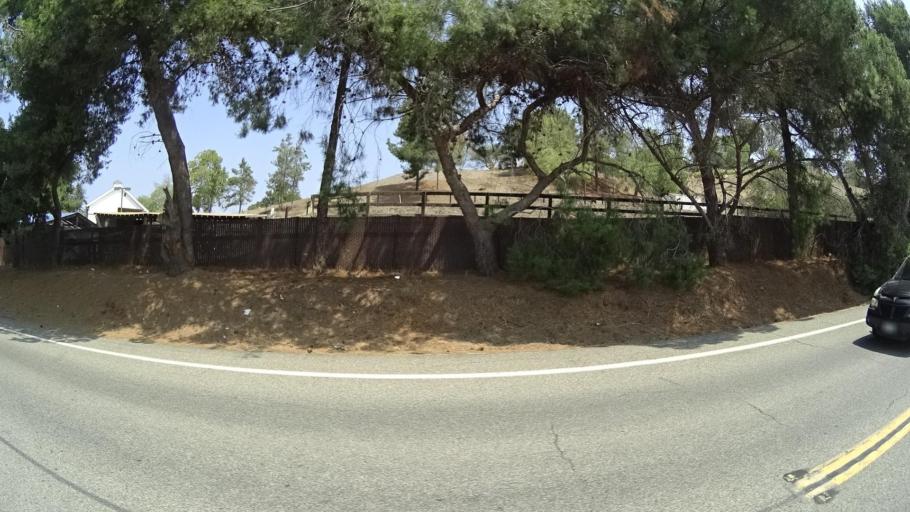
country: US
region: California
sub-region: San Diego County
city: Rainbow
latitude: 33.3935
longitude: -117.1992
